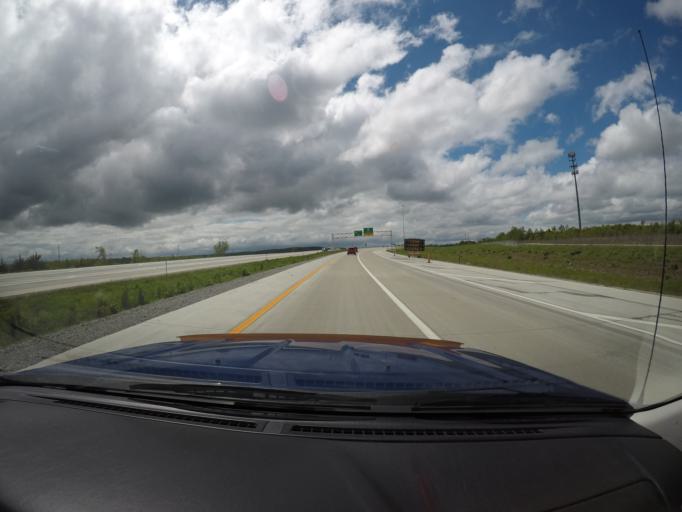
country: US
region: Kansas
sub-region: Douglas County
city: Lawrence
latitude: 38.9207
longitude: -95.2541
